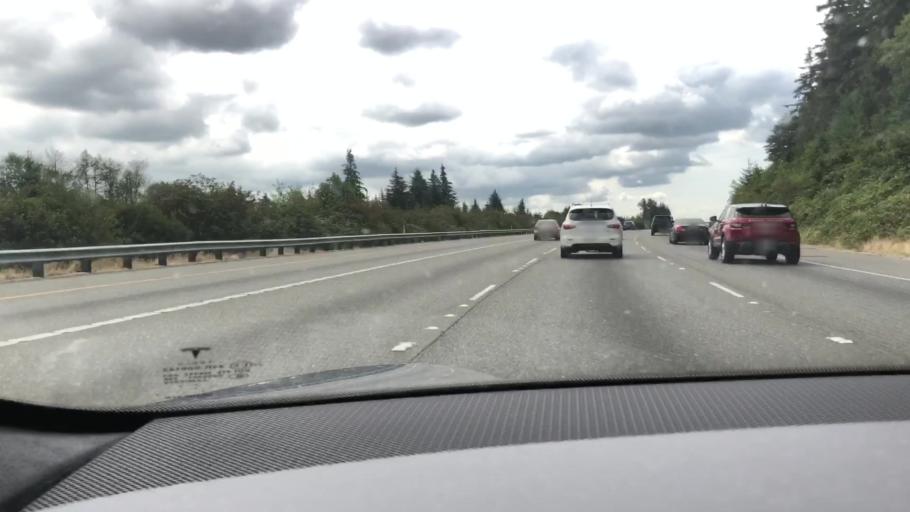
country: US
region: Washington
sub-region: Snohomish County
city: Martha Lake
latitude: 47.8625
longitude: -122.2457
